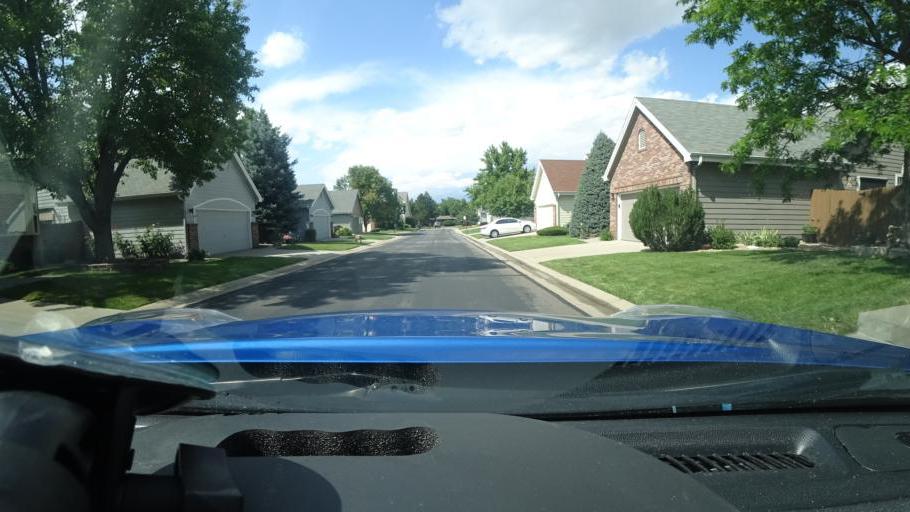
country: US
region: Colorado
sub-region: Adams County
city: Aurora
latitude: 39.6757
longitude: -104.8593
